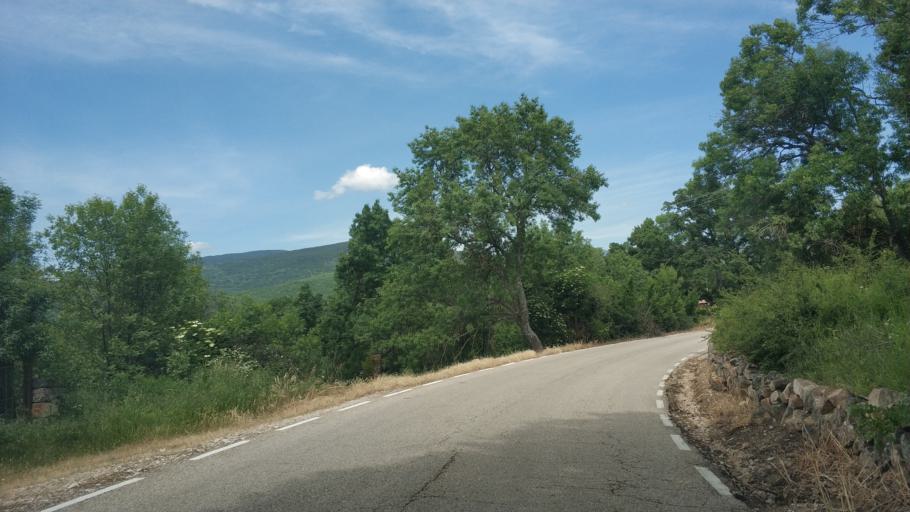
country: ES
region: Castille and Leon
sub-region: Provincia de Soria
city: Sotillo del Rincon
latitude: 41.8970
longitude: -2.6384
